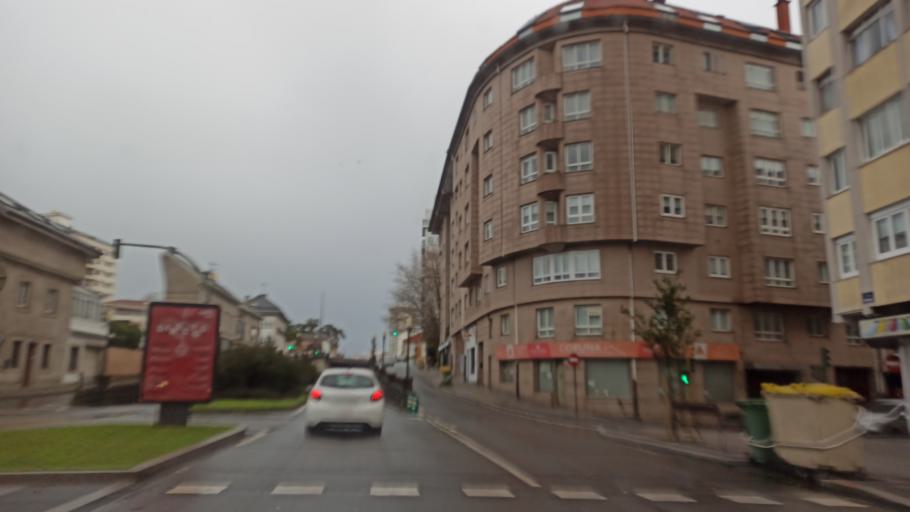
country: ES
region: Galicia
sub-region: Provincia da Coruna
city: A Coruna
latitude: 43.3579
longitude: -8.4125
